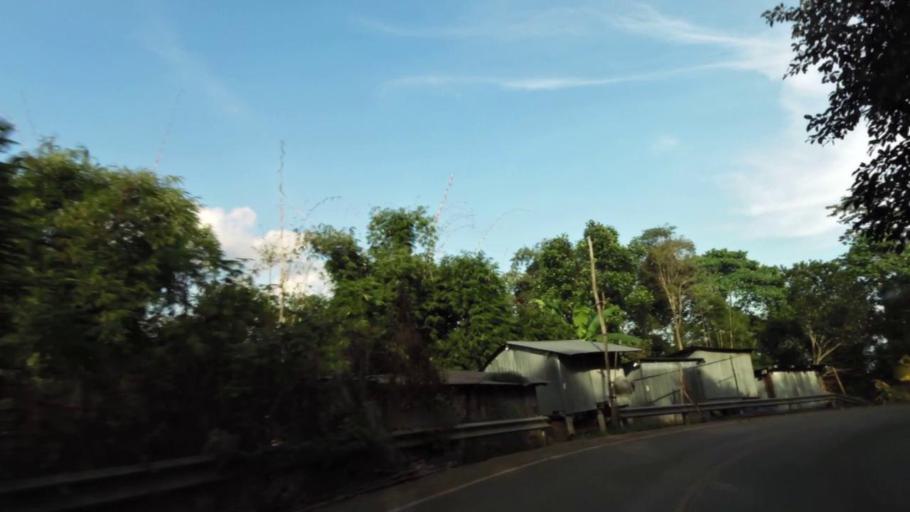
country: TH
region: Chiang Rai
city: Khun Tan
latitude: 19.8737
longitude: 100.3432
